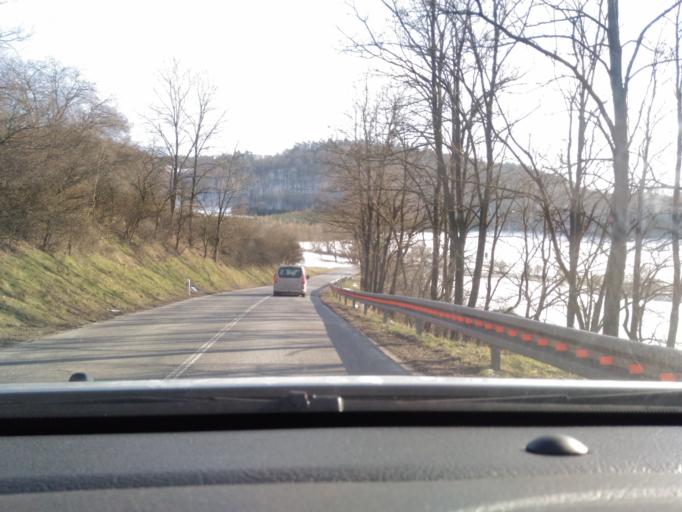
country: CZ
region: South Moravian
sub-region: Okres Brno-Venkov
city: Dolni Loucky
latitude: 49.4101
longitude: 16.3513
